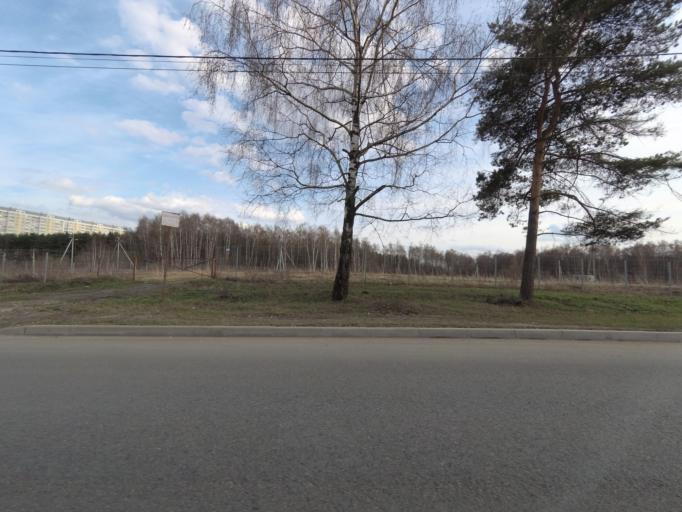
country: RU
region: Moskovskaya
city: Lobnya
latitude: 56.0021
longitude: 37.4265
